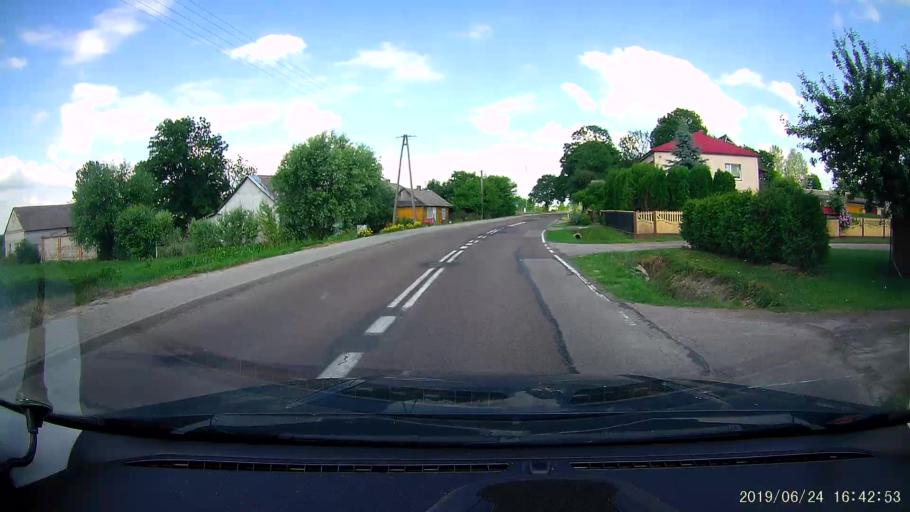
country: PL
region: Lublin Voivodeship
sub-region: Powiat tomaszowski
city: Michalow
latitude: 50.5348
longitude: 23.6240
